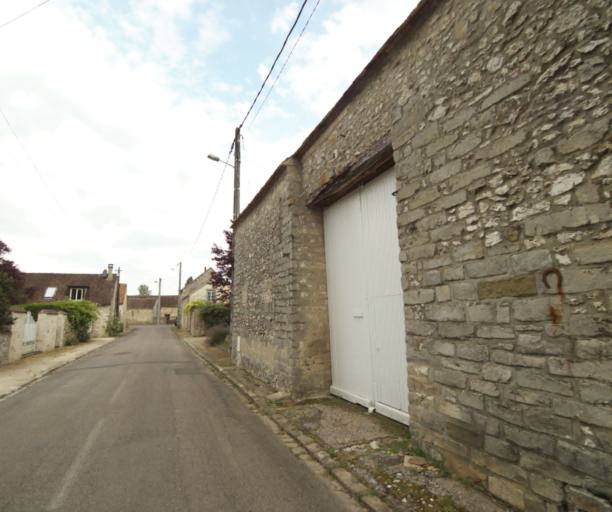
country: FR
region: Ile-de-France
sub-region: Departement de Seine-et-Marne
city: Cely
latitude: 48.4602
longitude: 2.5343
